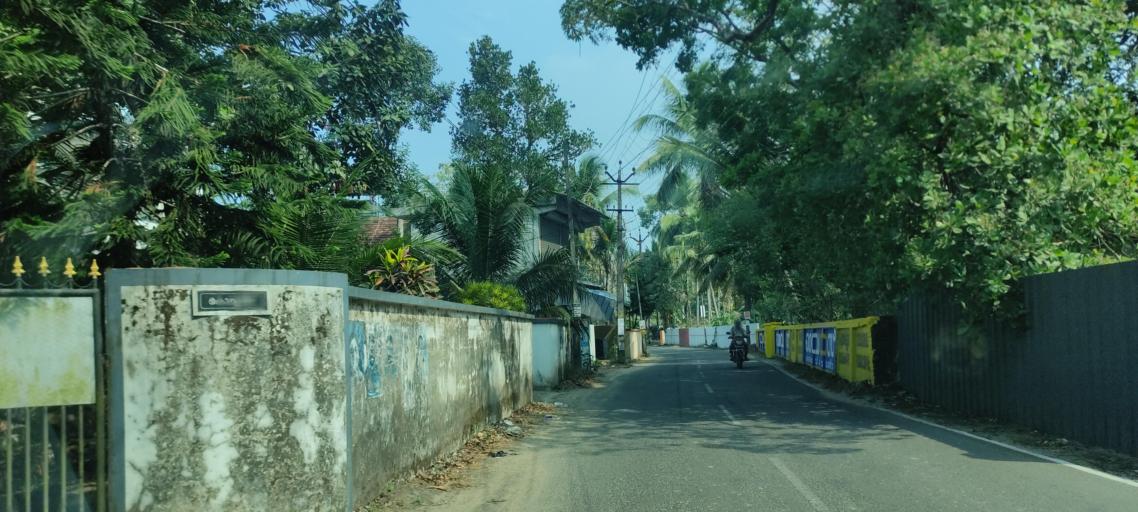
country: IN
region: Kerala
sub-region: Alappuzha
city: Kutiatodu
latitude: 9.7922
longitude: 76.3029
